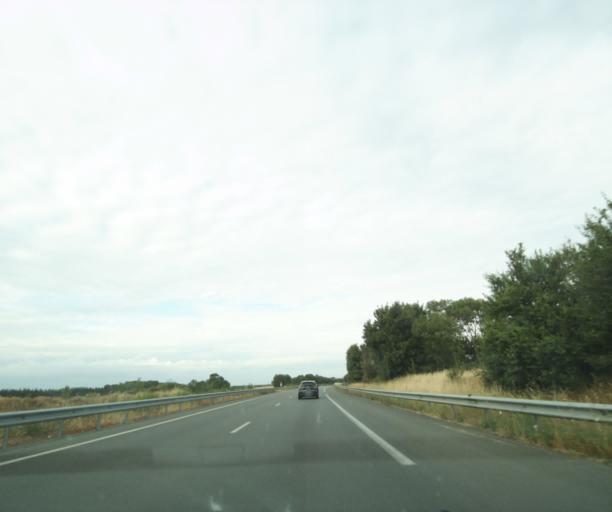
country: FR
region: Poitou-Charentes
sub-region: Departement de la Charente-Maritime
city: Dompierre-sur-Mer
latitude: 46.1929
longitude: -1.0664
